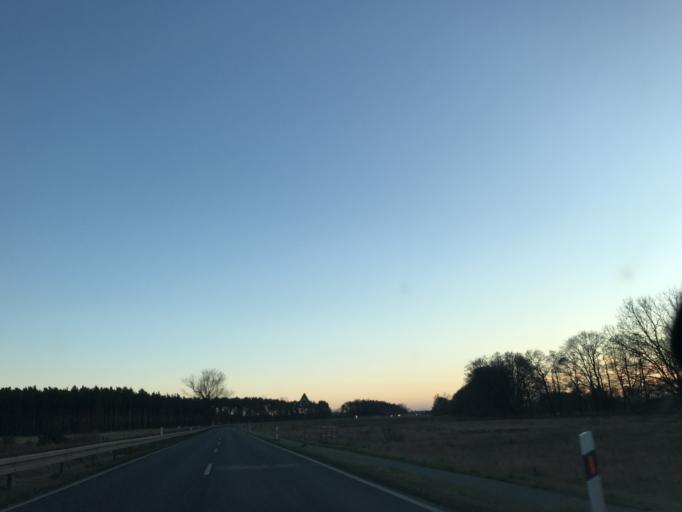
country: DE
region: Brandenburg
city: Premnitz
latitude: 52.5503
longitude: 12.3285
